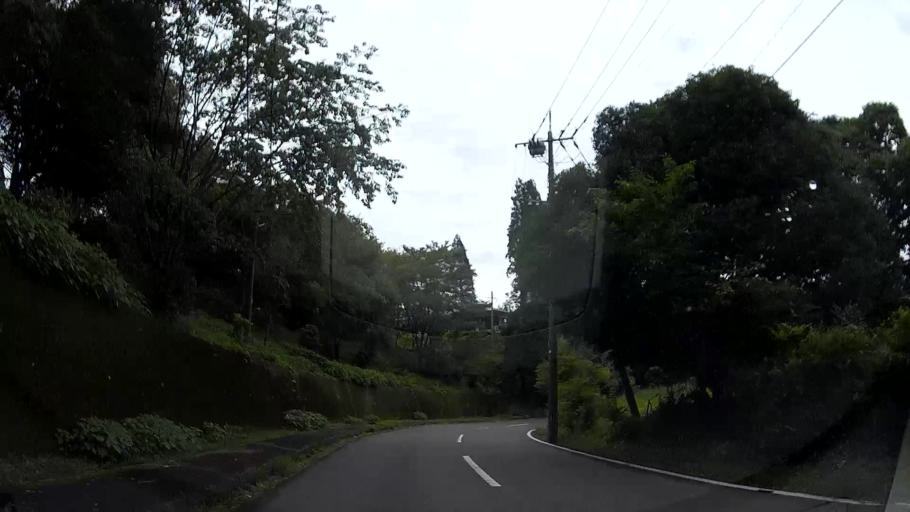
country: JP
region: Oita
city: Hita
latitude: 33.1396
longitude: 130.9737
